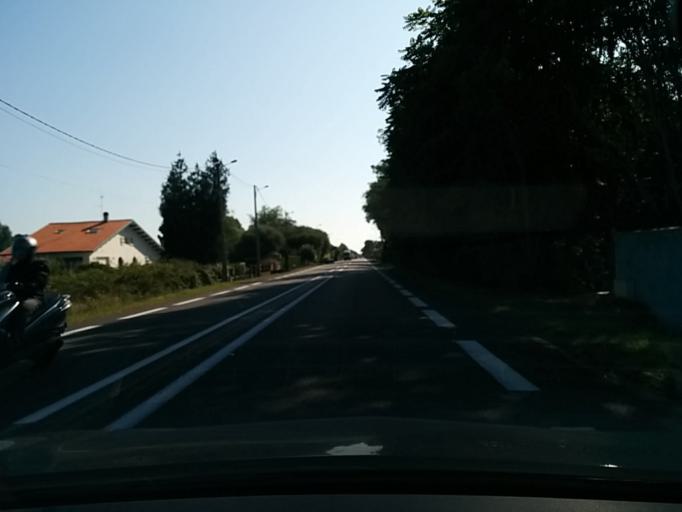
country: FR
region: Aquitaine
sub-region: Departement des Landes
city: Benesse-Maremne
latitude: 43.6319
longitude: -1.3635
